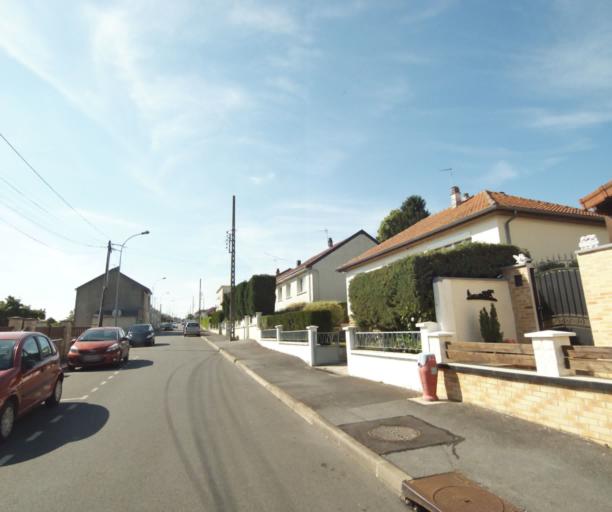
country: FR
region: Champagne-Ardenne
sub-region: Departement des Ardennes
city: Warcq
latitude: 49.7835
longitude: 4.6994
